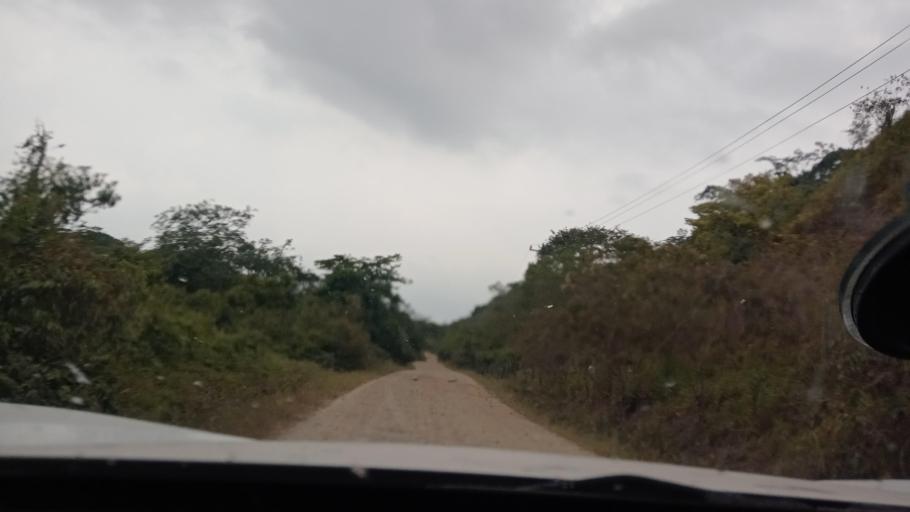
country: MX
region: Veracruz
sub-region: Uxpanapa
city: Poblado 10
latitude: 17.4540
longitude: -94.0897
